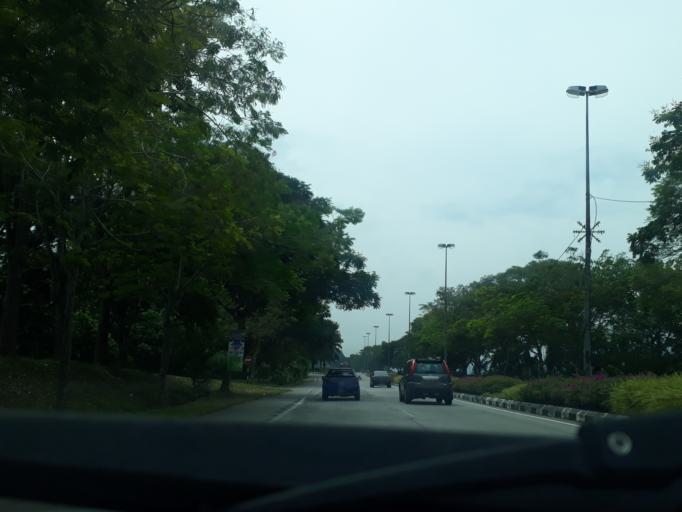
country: MY
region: Perak
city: Ipoh
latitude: 4.6329
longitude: 101.1541
